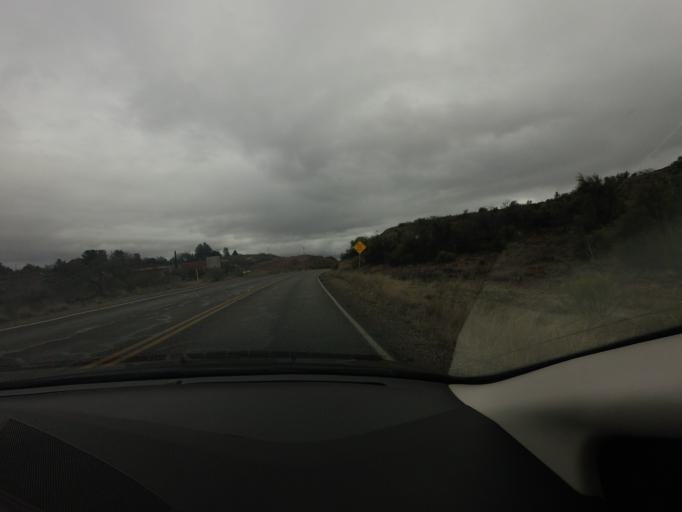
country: US
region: Arizona
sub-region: Yavapai County
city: Clarkdale
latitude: 34.7629
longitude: -112.0408
